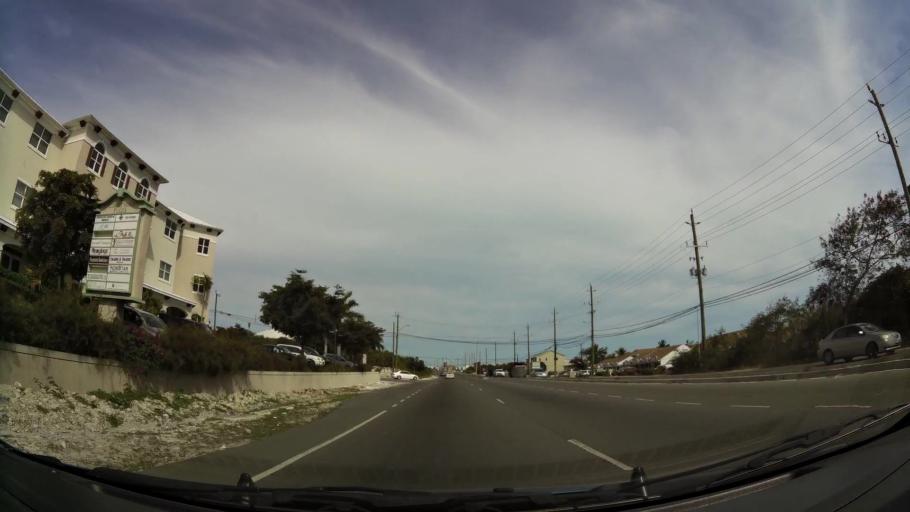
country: BS
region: Mayaguana
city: Abraham's Bay
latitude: 21.7789
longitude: -72.2343
